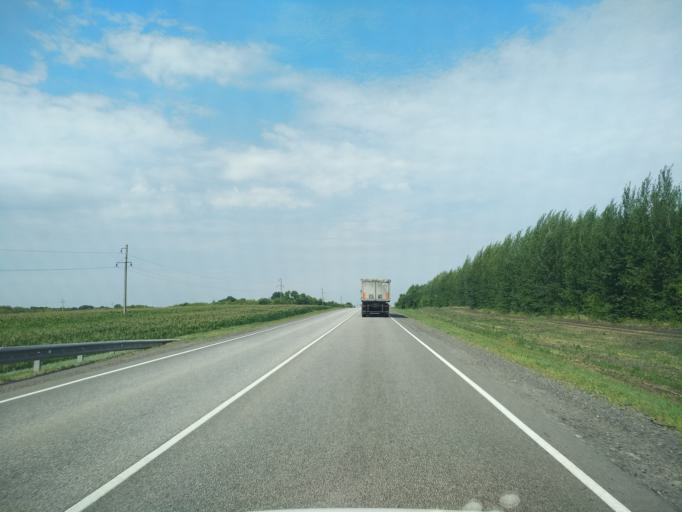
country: RU
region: Voronezj
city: Orlovo
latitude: 51.6761
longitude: 39.7183
